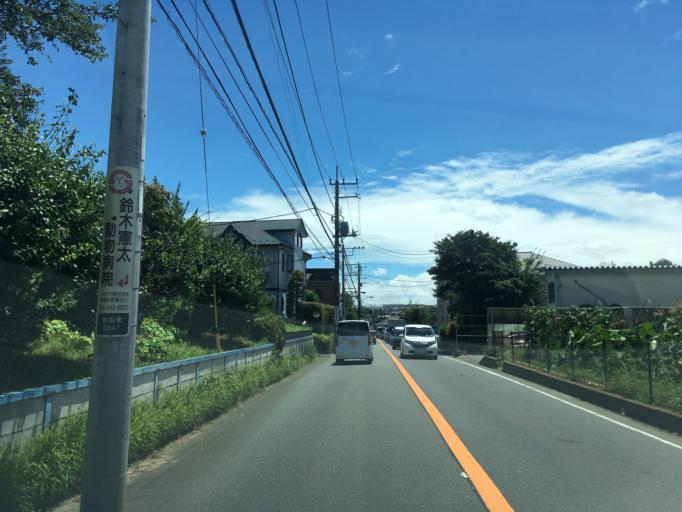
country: JP
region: Tokyo
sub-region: Machida-shi
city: Machida
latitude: 35.5420
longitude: 139.4967
